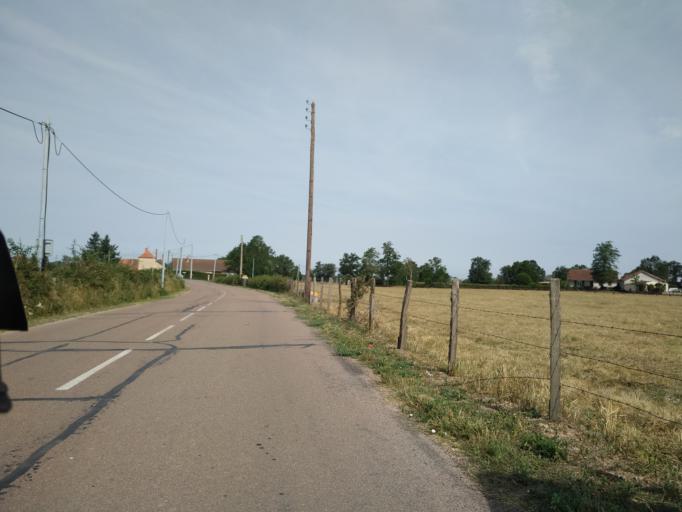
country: FR
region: Bourgogne
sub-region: Departement de Saone-et-Loire
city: Saint-Yan
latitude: 46.3539
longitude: 4.0084
